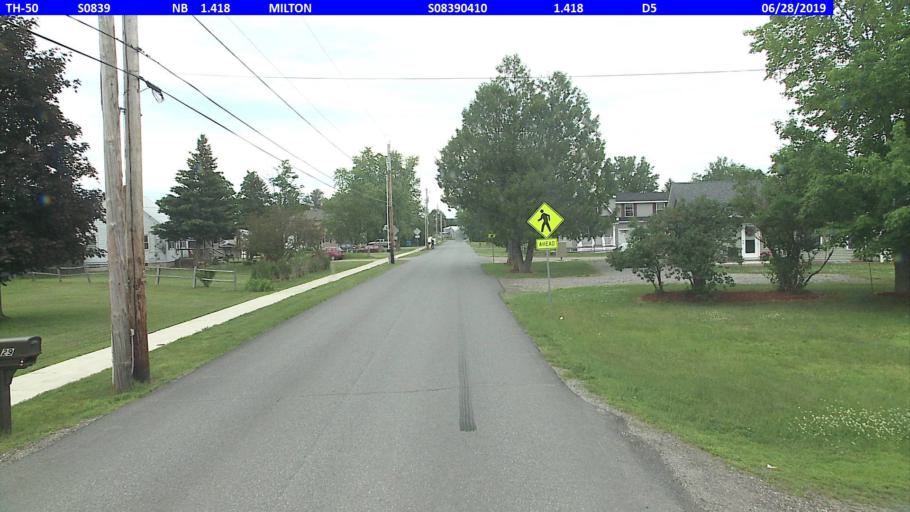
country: US
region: Vermont
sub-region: Chittenden County
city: Milton
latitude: 44.6238
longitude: -73.1118
